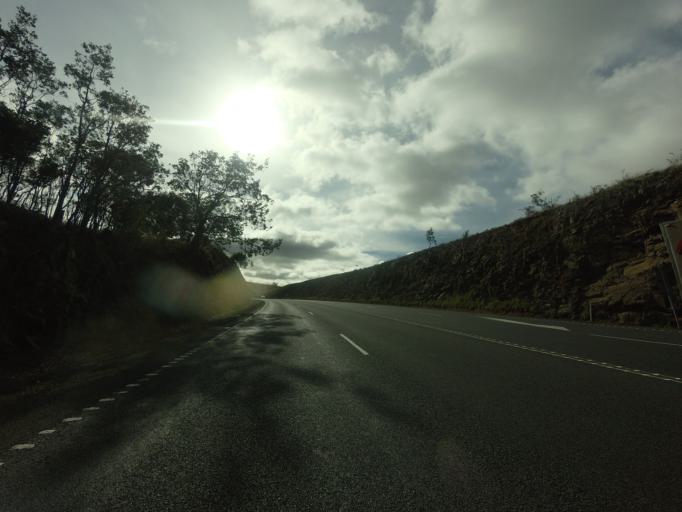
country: AU
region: Tasmania
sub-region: Brighton
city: Bridgewater
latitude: -42.4106
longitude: 147.2626
